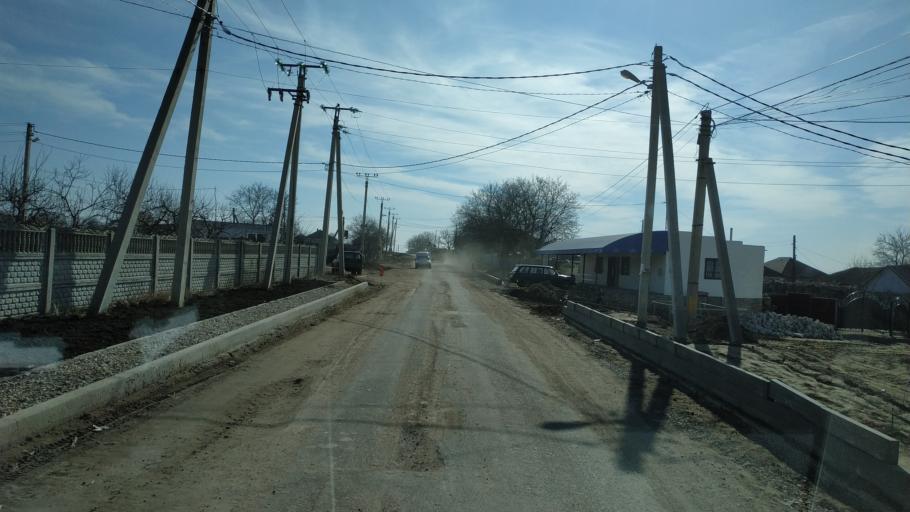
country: MD
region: Nisporeni
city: Nisporeni
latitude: 47.2169
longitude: 28.0549
